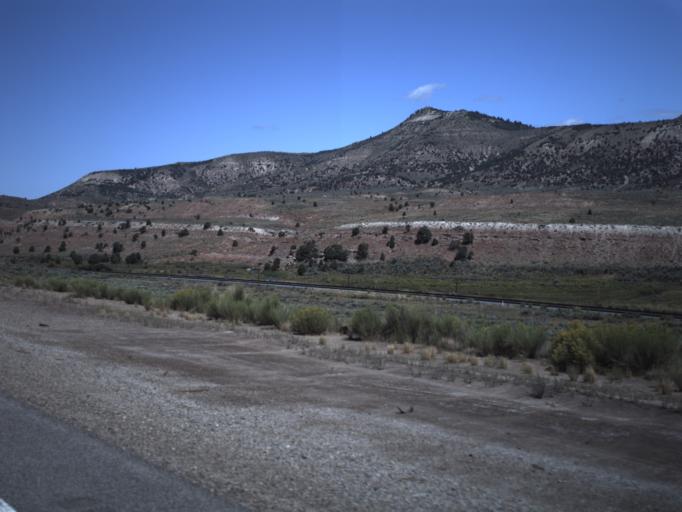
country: US
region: Utah
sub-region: Carbon County
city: Helper
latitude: 39.8379
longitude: -110.9813
